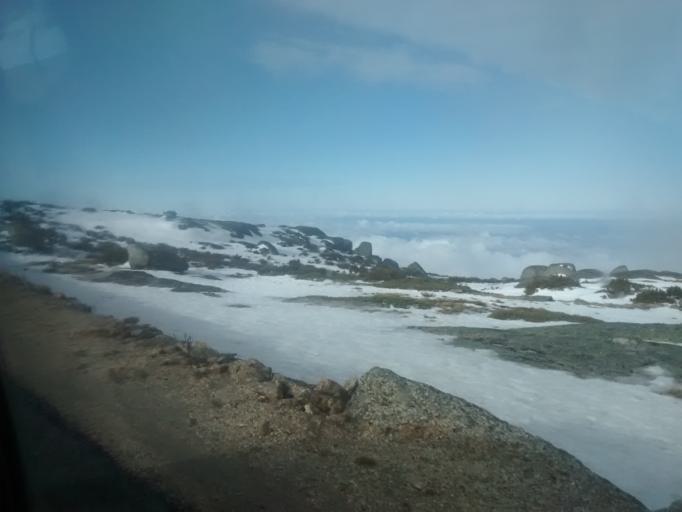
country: PT
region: Guarda
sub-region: Seia
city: Seia
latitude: 40.3482
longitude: -7.6627
